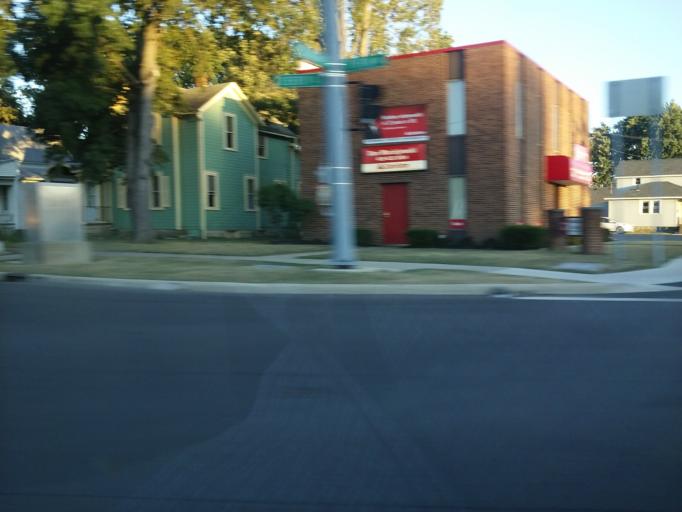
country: US
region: Ohio
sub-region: Hancock County
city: Findlay
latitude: 41.0454
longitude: -83.6413
